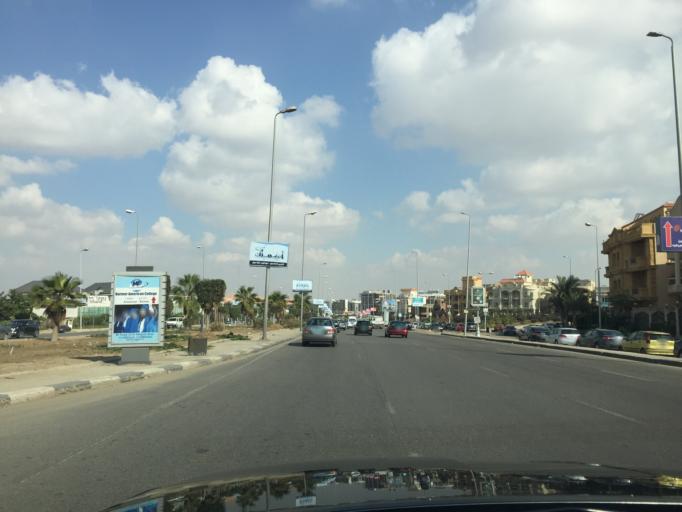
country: EG
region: Muhafazat al Qalyubiyah
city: Al Khankah
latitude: 30.0217
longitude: 31.4521
